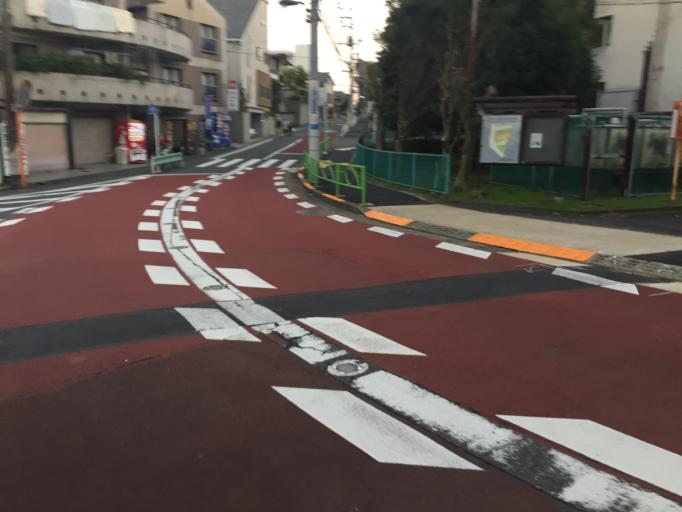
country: JP
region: Tokyo
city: Tokyo
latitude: 35.6283
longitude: 139.6678
